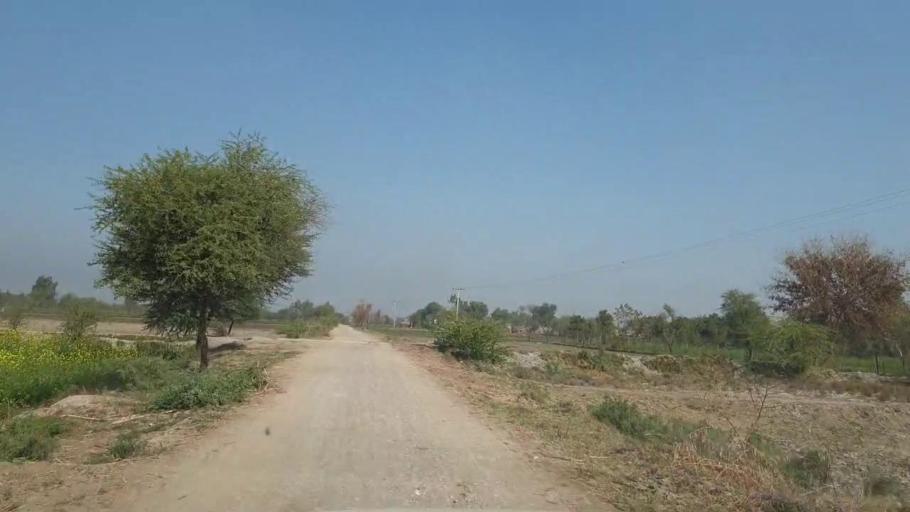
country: PK
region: Sindh
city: Mirpur Khas
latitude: 25.5116
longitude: 69.1240
